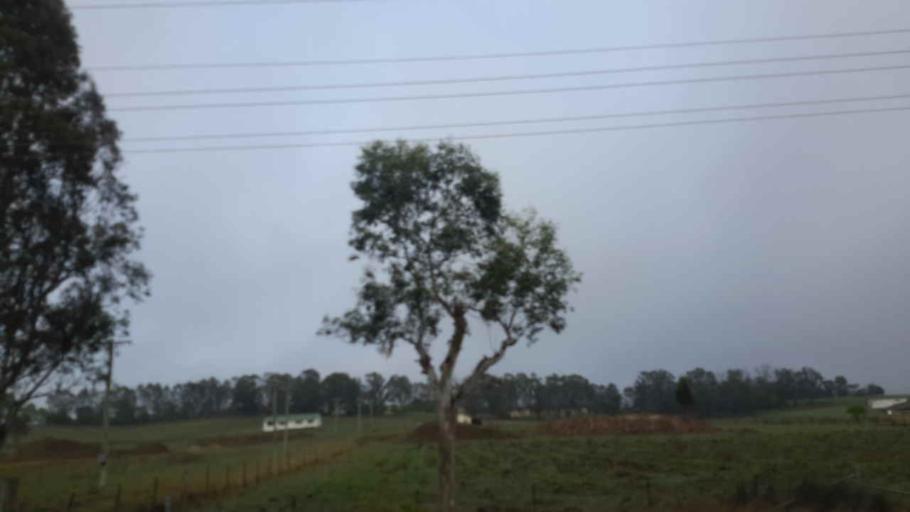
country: AU
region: New South Wales
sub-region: Penrith Municipality
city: Glenmore Park
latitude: -33.7995
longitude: 150.6978
